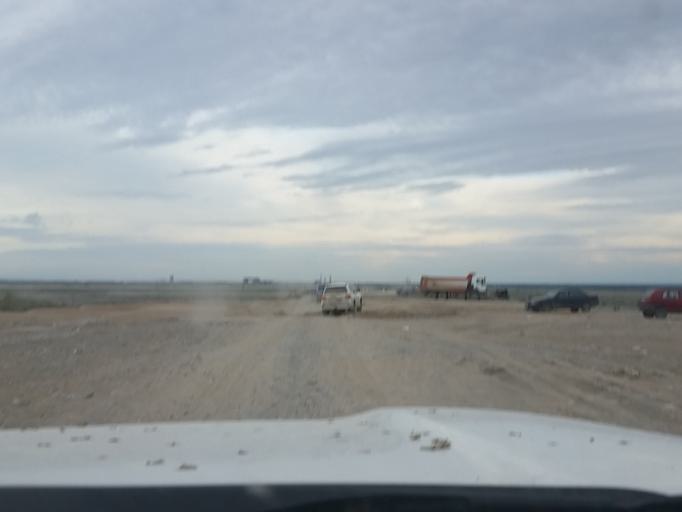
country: KZ
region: Almaty Oblysy
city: Zharkent
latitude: 44.1724
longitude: 80.3457
